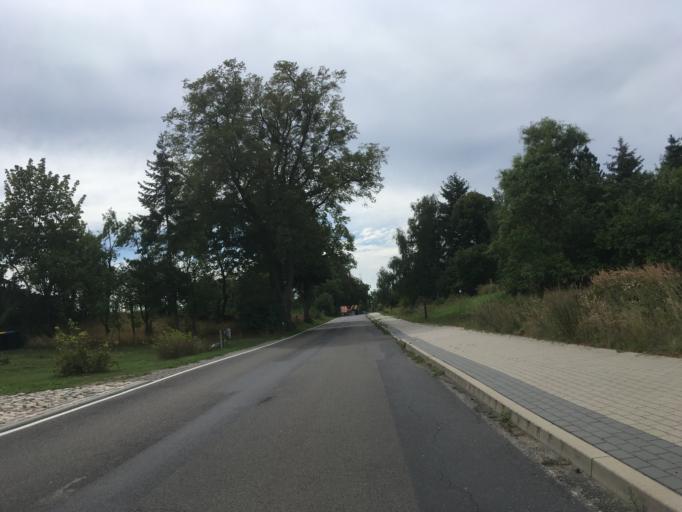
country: DE
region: Brandenburg
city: Mittenwalde
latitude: 53.2251
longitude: 13.6611
